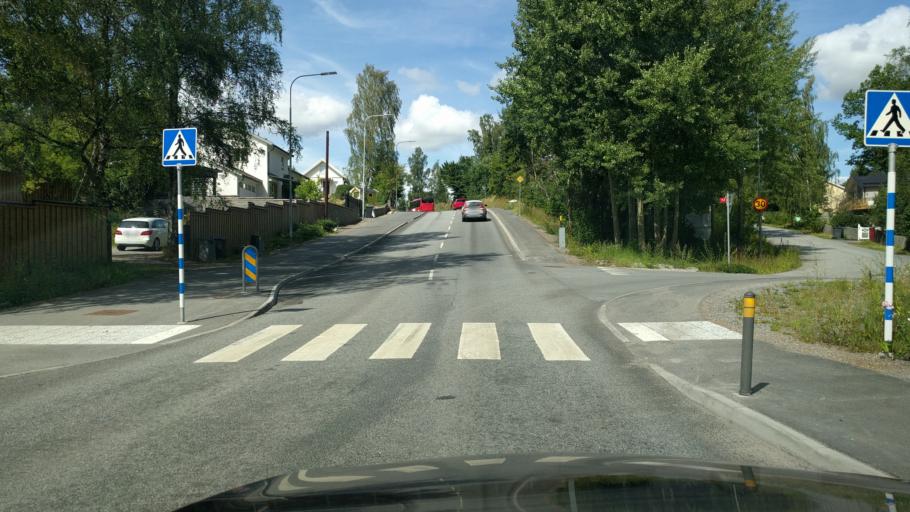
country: SE
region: Stockholm
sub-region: Taby Kommun
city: Taby
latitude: 59.4493
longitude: 18.0623
